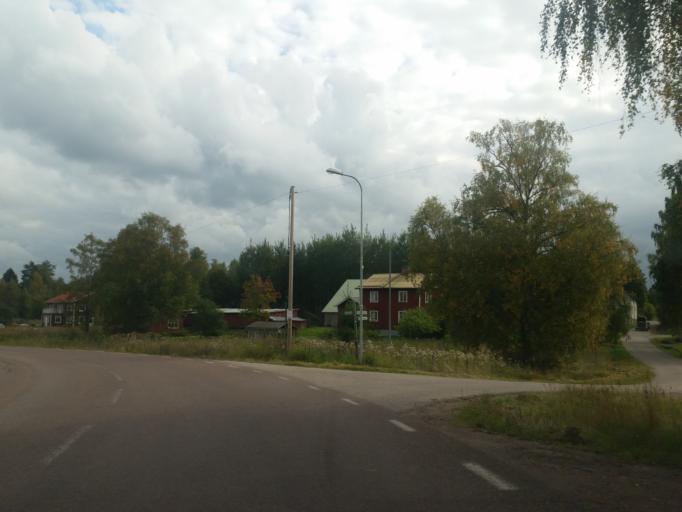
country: SE
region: Dalarna
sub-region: Leksand Municipality
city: Smedby
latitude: 60.6782
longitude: 15.1217
